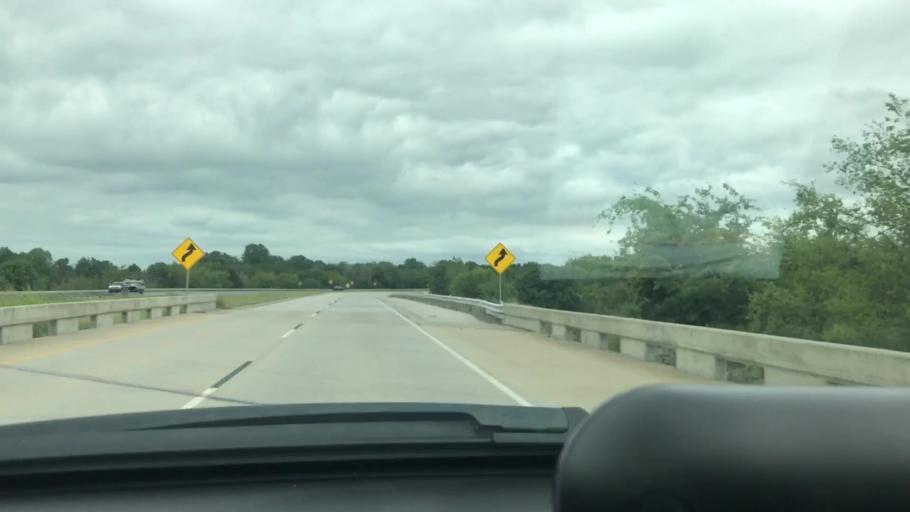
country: US
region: Oklahoma
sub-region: Wagoner County
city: Wagoner
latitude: 35.9086
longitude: -95.4026
